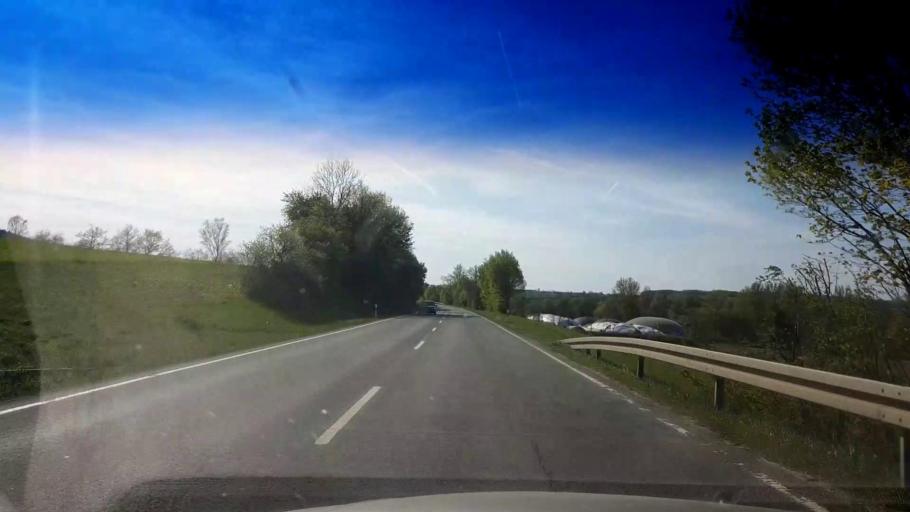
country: DE
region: Bavaria
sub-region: Upper Franconia
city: Eggolsheim
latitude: 49.8060
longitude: 11.0706
